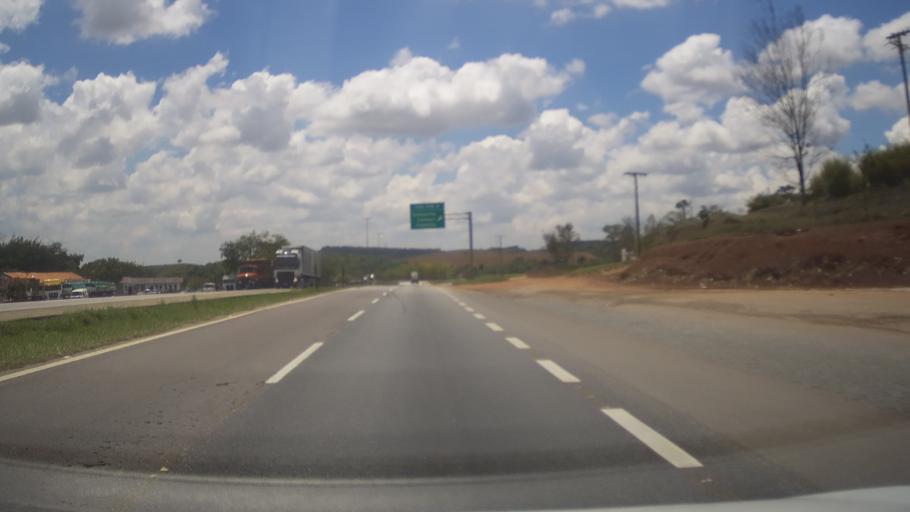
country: BR
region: Minas Gerais
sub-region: Campanha
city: Campanha
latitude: -21.7889
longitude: -45.4416
